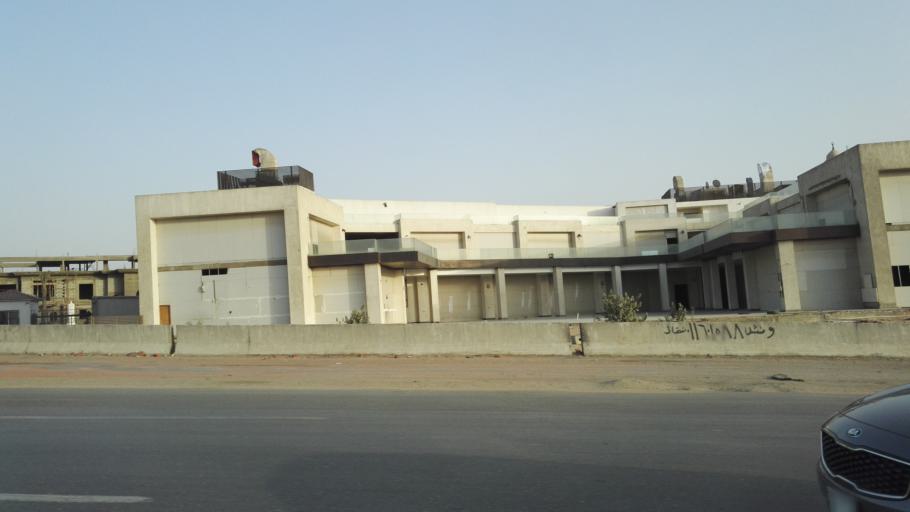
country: EG
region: Muhafazat al Qahirah
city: Cairo
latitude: 29.9945
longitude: 31.3879
